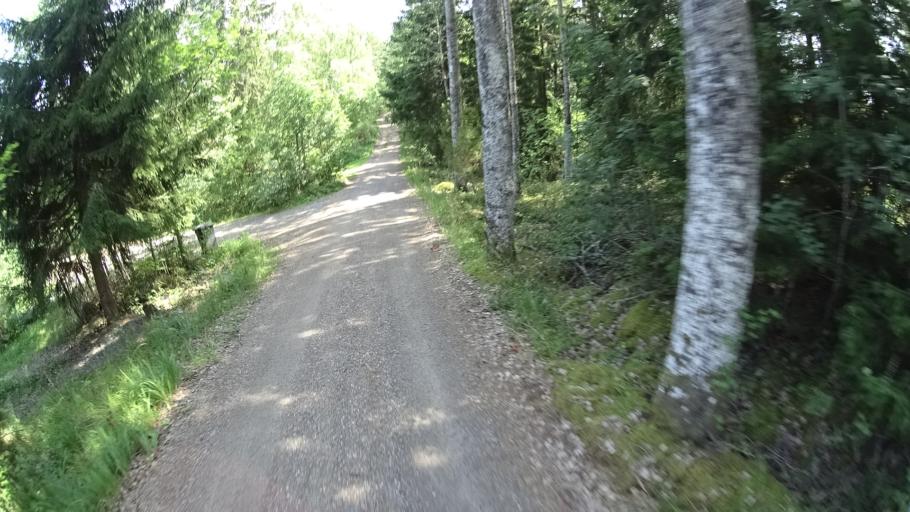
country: FI
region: Haeme
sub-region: Forssa
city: Tammela
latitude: 60.7688
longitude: 23.8758
